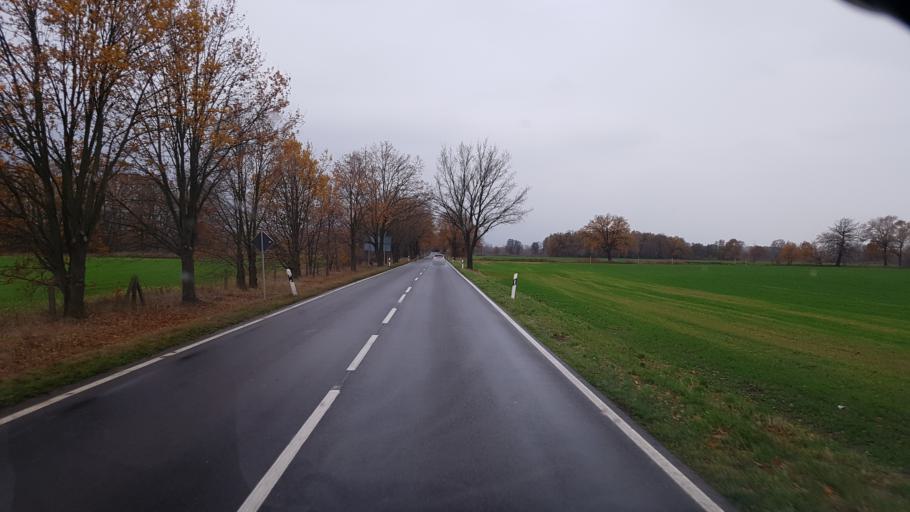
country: DE
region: Brandenburg
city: Schraden
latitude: 51.4655
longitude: 13.7126
